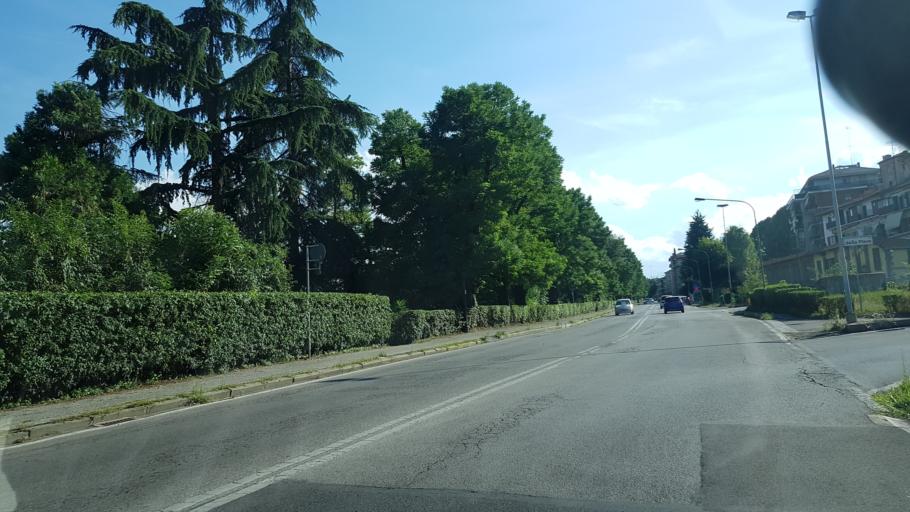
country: IT
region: Piedmont
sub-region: Provincia di Cuneo
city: Cuneo
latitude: 44.3907
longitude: 7.5531
